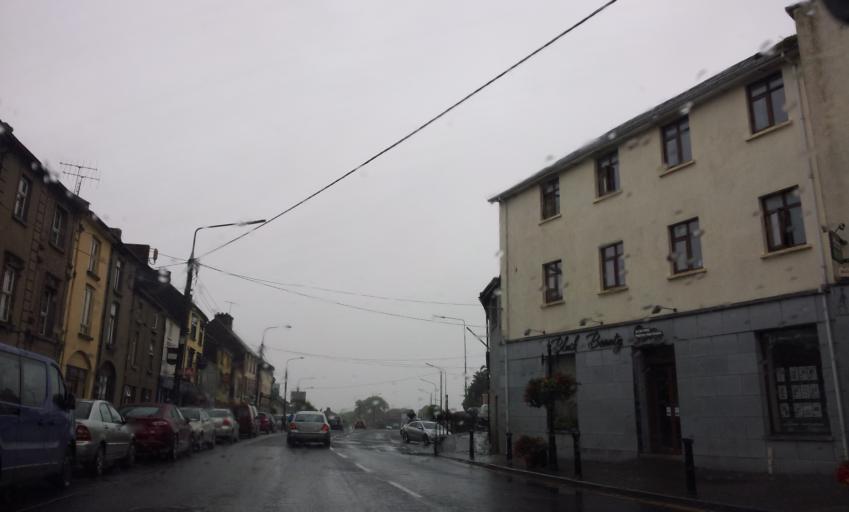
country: IE
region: Munster
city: Cashel
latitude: 52.5183
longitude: -7.8861
